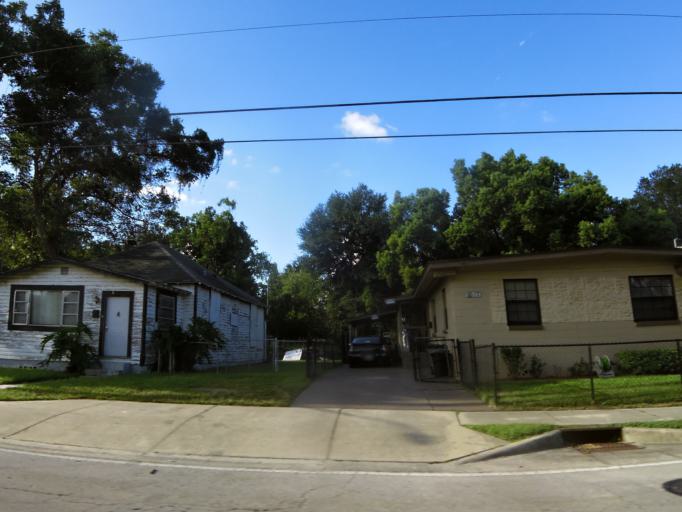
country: US
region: Florida
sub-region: Duval County
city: Jacksonville
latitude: 30.3513
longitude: -81.6834
